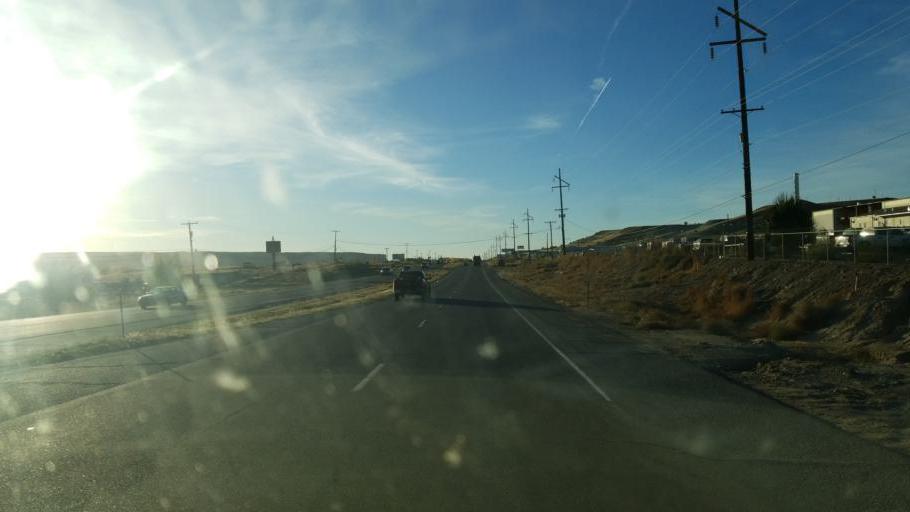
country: US
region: New Mexico
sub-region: San Juan County
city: Lee Acres
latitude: 36.7045
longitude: -108.1075
